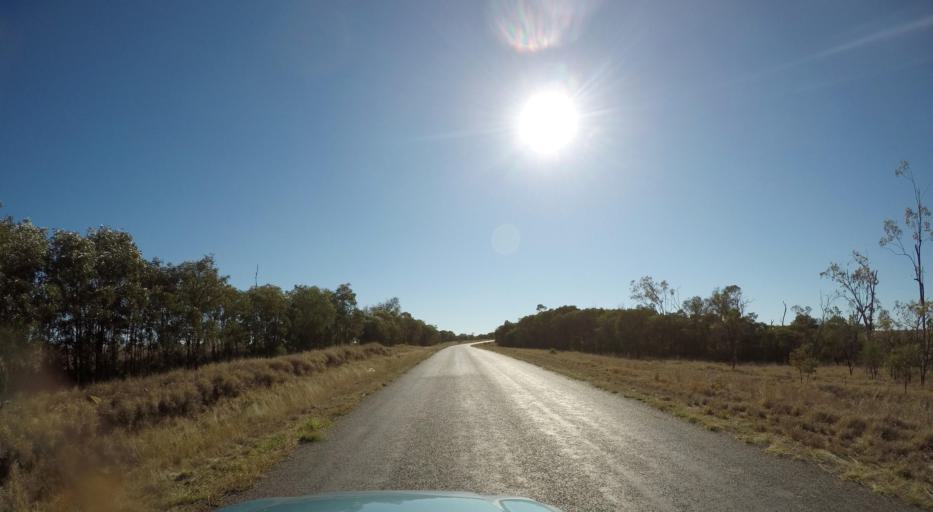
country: AU
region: Queensland
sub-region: Banana
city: Taroom
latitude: -25.9973
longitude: 149.3588
